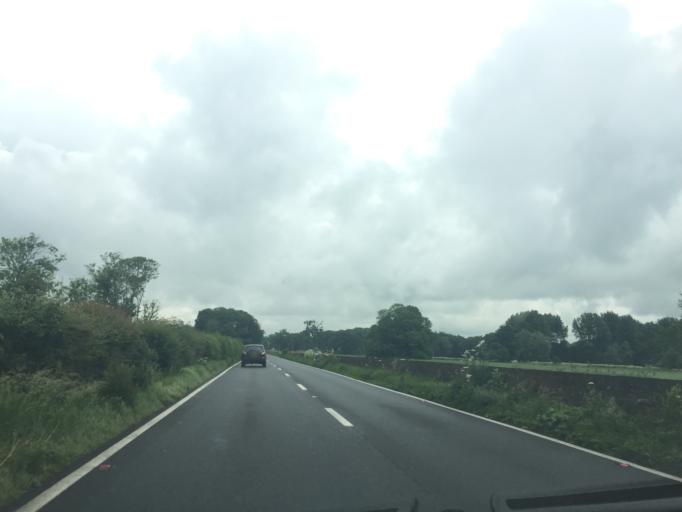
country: GB
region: England
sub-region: Dorset
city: Lytchett Matravers
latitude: 50.7850
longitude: -2.1287
